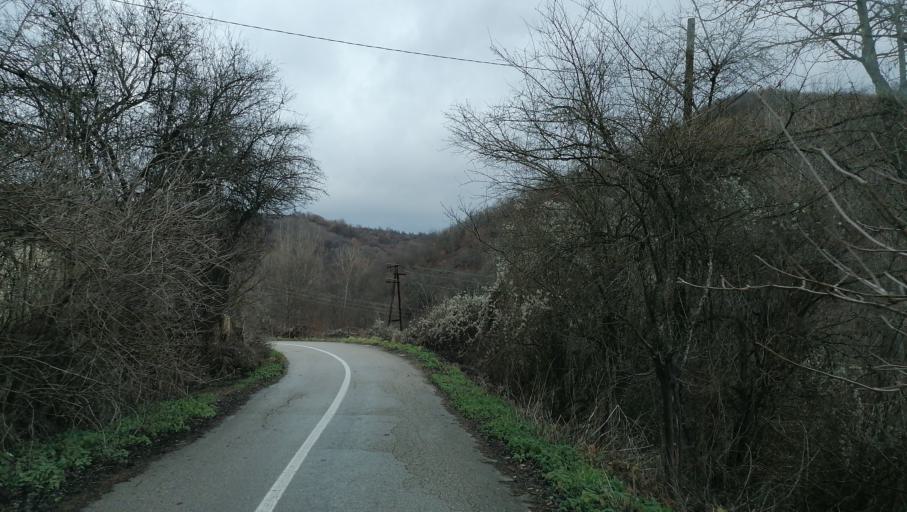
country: RS
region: Central Serbia
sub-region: Pirotski Okrug
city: Dimitrovgrad
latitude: 42.9257
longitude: 22.7558
